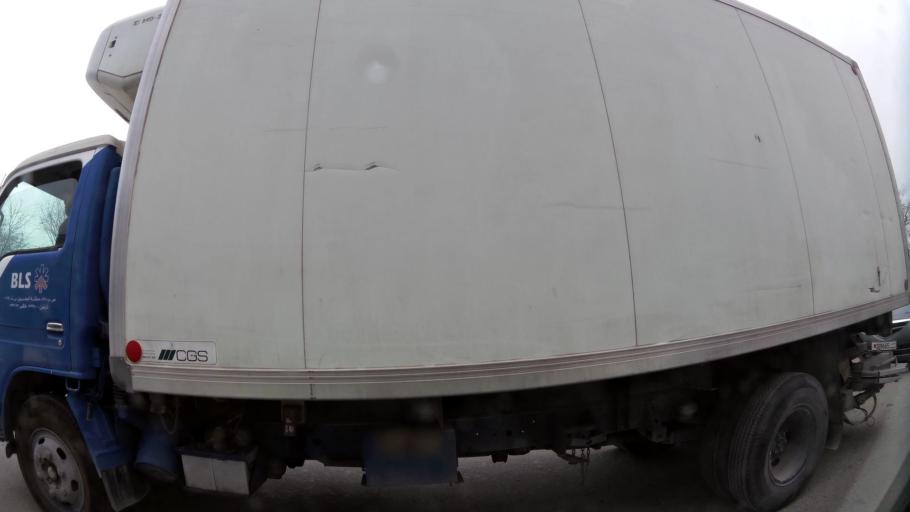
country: BH
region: Northern
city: Madinat `Isa
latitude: 26.1858
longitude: 50.5347
